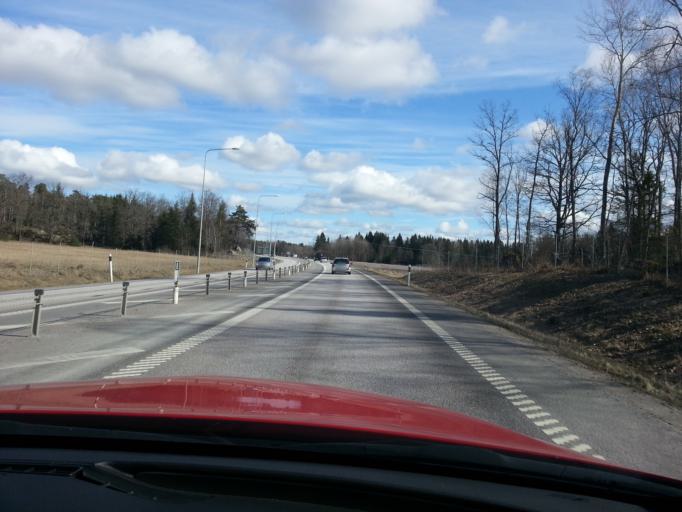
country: SE
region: Uppsala
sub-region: Uppsala Kommun
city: Storvreta
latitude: 59.9250
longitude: 17.7789
